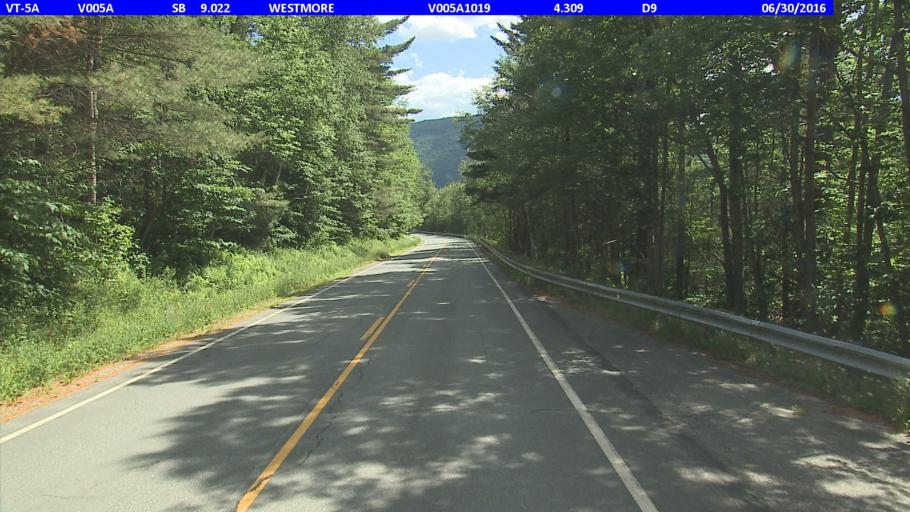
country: US
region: Vermont
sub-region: Caledonia County
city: Lyndonville
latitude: 44.7525
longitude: -72.0526
